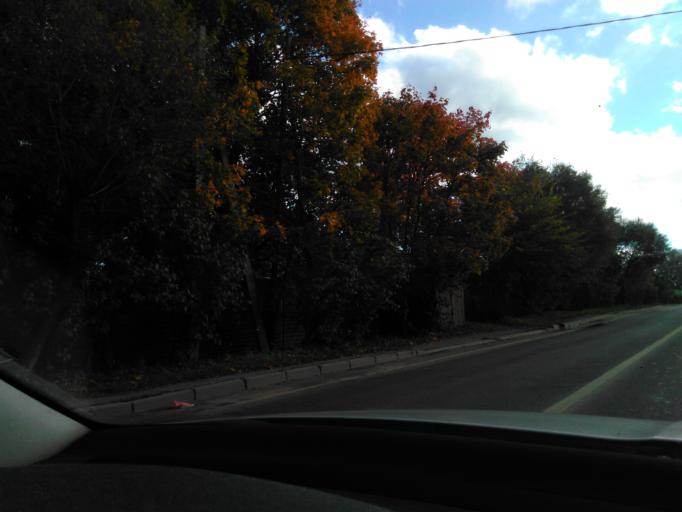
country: RU
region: Moskovskaya
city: Solnechnogorsk
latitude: 56.0943
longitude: 36.9126
